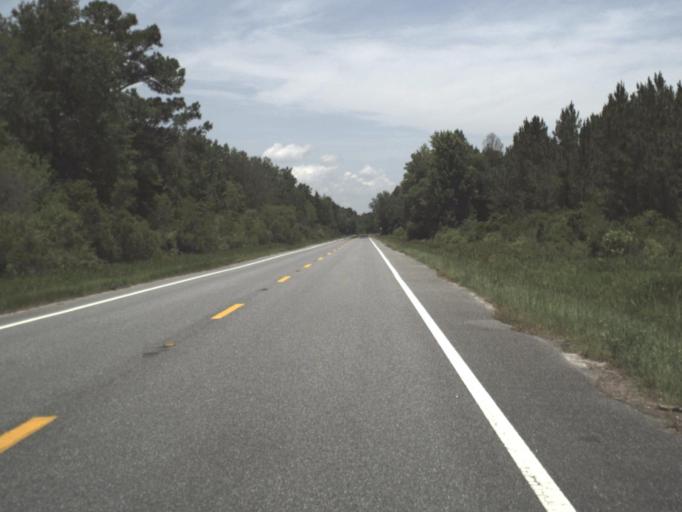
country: US
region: Florida
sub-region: Taylor County
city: Steinhatchee
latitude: 29.8713
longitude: -83.3072
